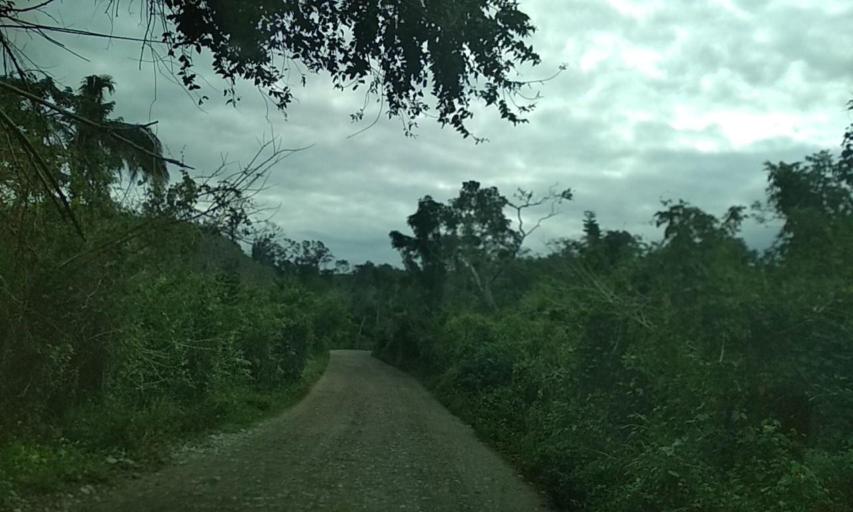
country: MX
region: Veracruz
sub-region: Papantla
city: Residencial Tajin
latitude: 20.6303
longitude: -97.3650
